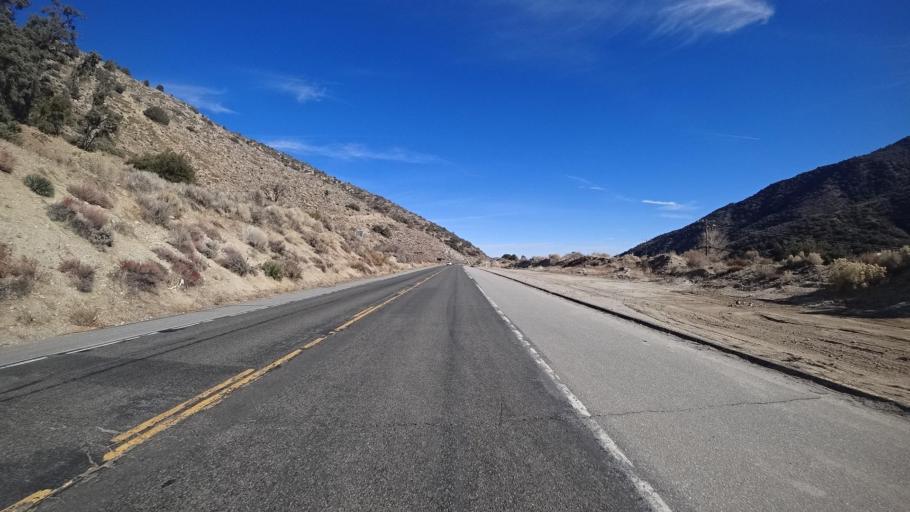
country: US
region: California
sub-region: Kern County
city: Frazier Park
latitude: 34.8202
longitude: -118.9753
